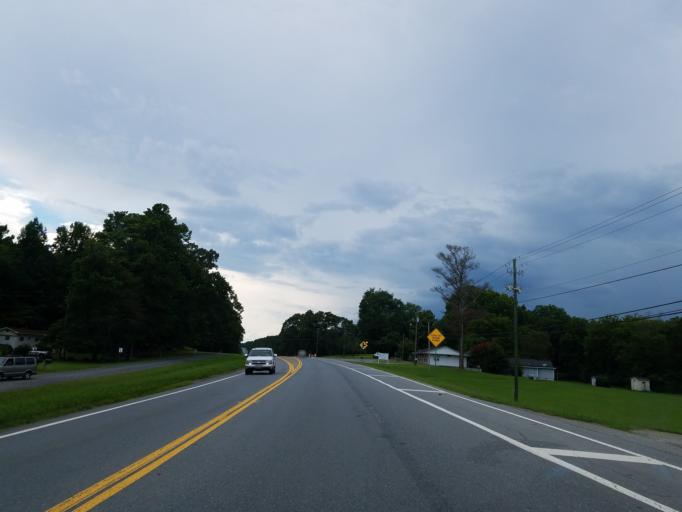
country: US
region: Georgia
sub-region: Bartow County
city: Adairsville
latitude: 34.2834
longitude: -84.8695
